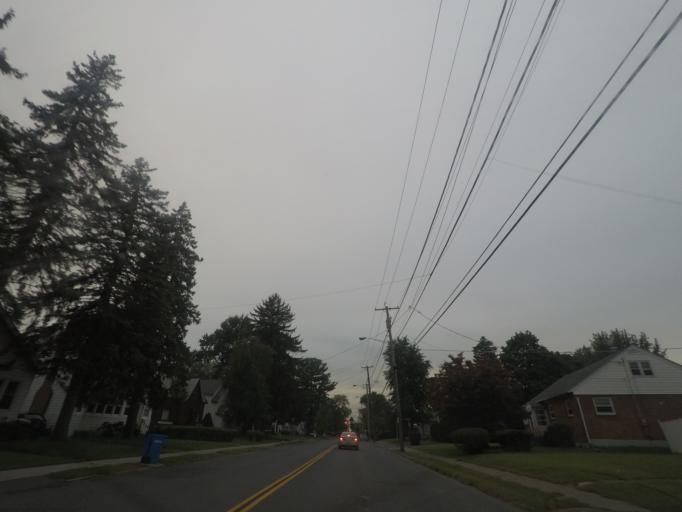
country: US
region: New York
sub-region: Albany County
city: Albany
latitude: 42.6455
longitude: -73.7961
